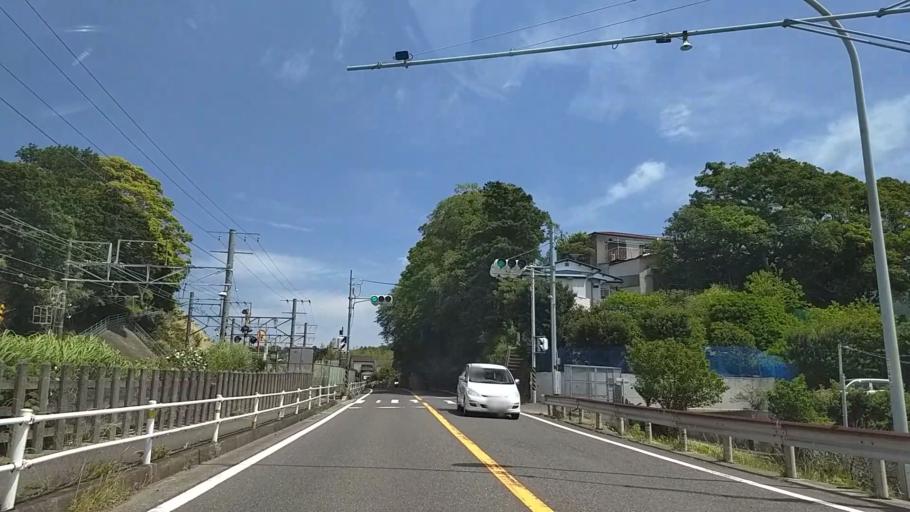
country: JP
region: Kanagawa
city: Yugawara
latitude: 35.1601
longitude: 139.1355
